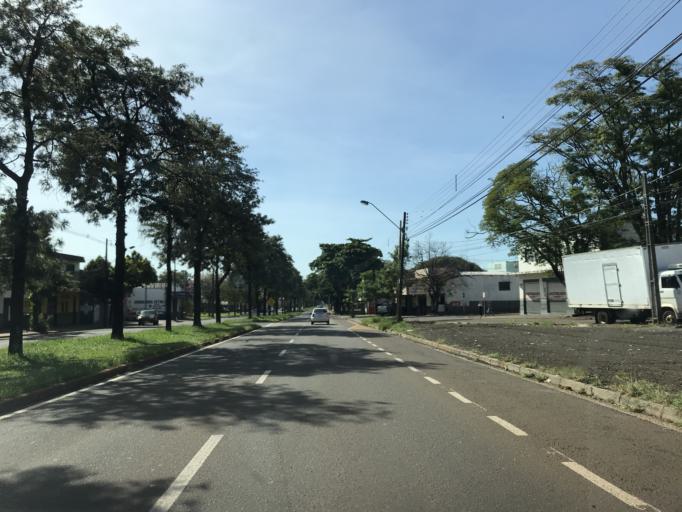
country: BR
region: Parana
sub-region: Maringa
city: Maringa
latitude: -23.3954
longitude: -51.9247
